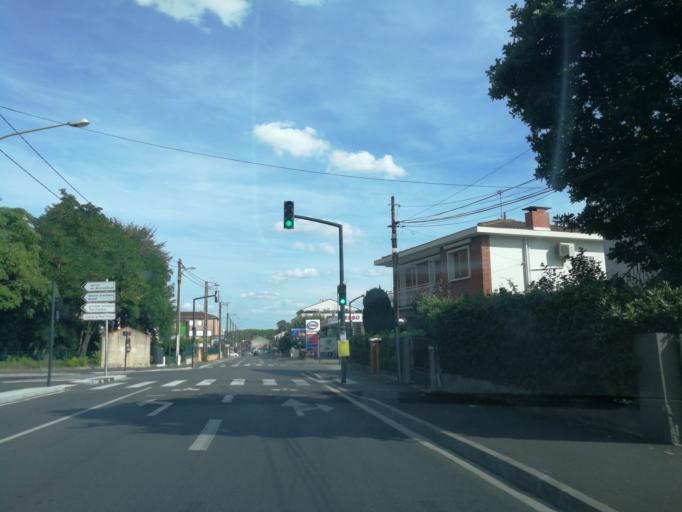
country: FR
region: Midi-Pyrenees
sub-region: Departement de la Haute-Garonne
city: Ramonville-Saint-Agne
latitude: 43.5755
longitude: 1.4888
